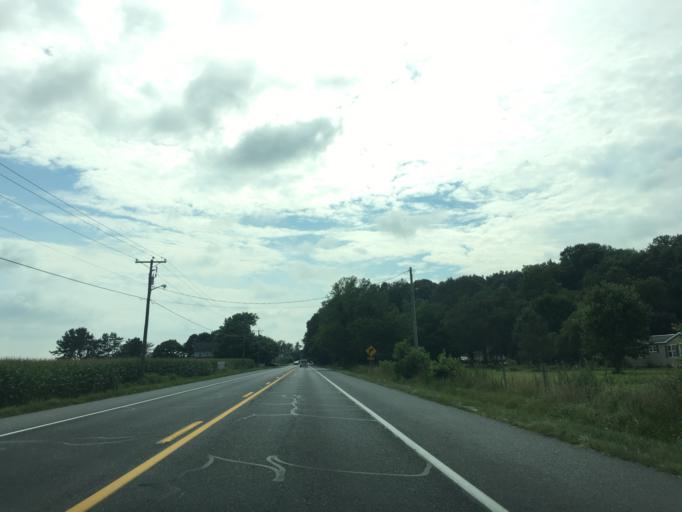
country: US
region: Delaware
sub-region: Sussex County
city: Long Neck
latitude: 38.5547
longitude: -75.1791
